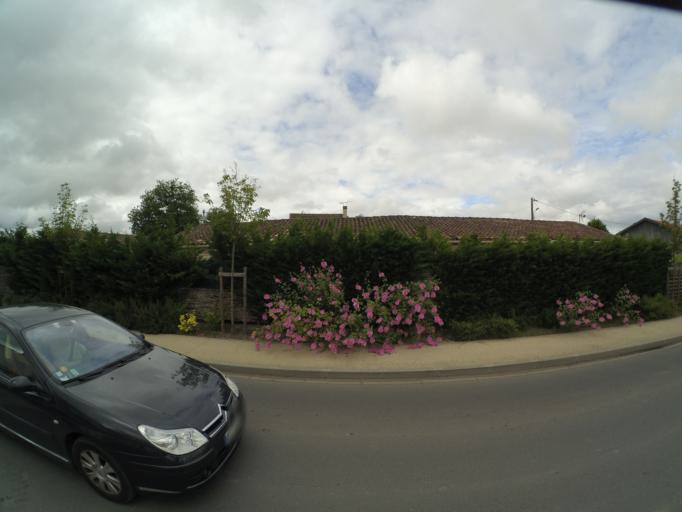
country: FR
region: Aquitaine
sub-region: Departement de la Gironde
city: Cantenac
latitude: 45.0283
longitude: -0.6524
